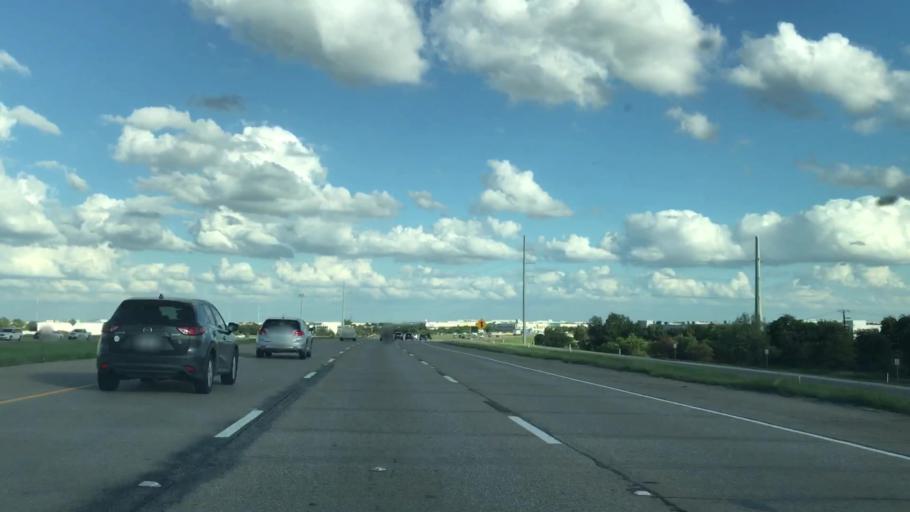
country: US
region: Texas
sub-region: Dallas County
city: Coppell
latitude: 32.9450
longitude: -97.0215
